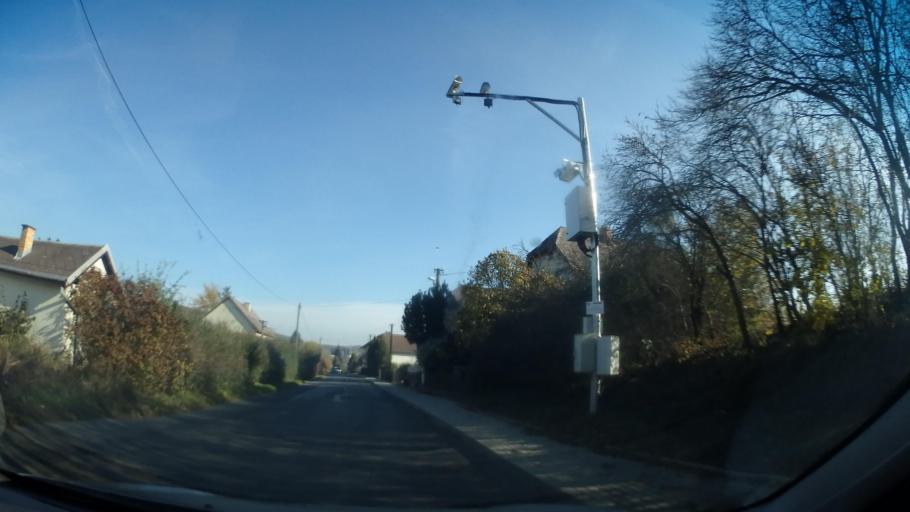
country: CZ
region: Central Bohemia
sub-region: Okres Praha-Vychod
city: Strancice
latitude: 49.9602
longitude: 14.6791
